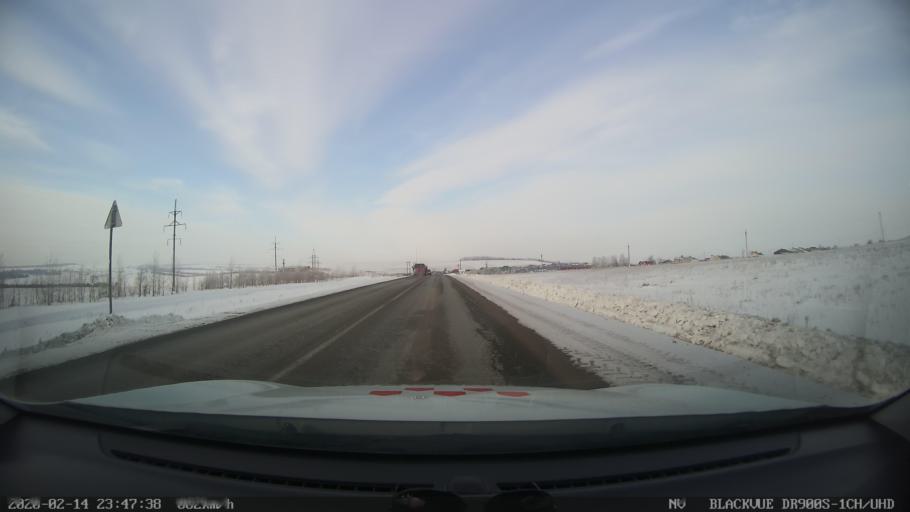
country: RU
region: Tatarstan
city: Kuybyshevskiy Zaton
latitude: 55.2407
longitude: 49.2081
